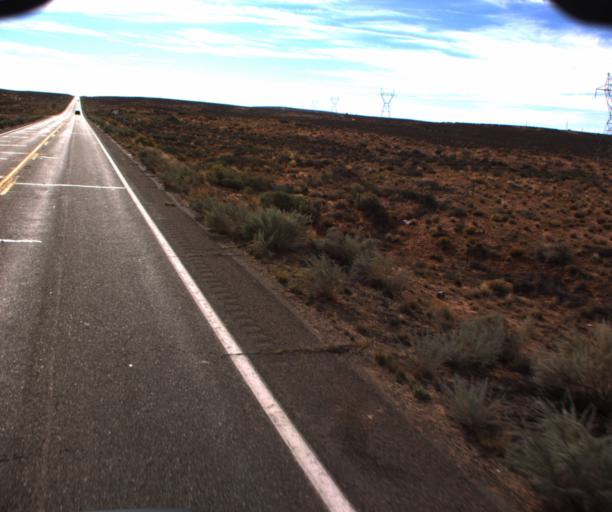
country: US
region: Arizona
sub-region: Coconino County
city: LeChee
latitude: 36.8420
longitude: -111.3270
